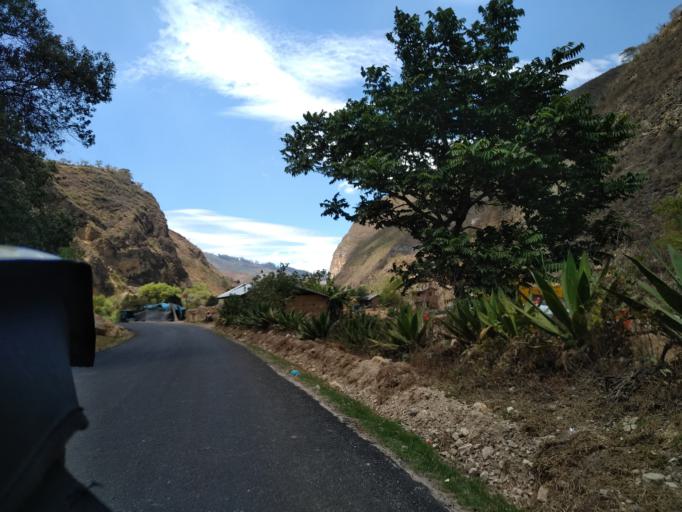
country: PE
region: Amazonas
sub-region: Provincia de Chachapoyas
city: Duraznopampa
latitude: -6.5763
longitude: -77.8264
